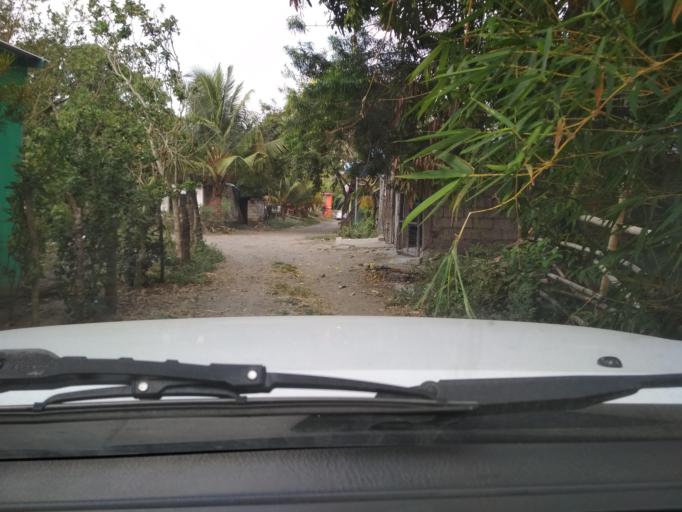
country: MX
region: Veracruz
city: El Tejar
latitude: 19.0836
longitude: -96.1657
